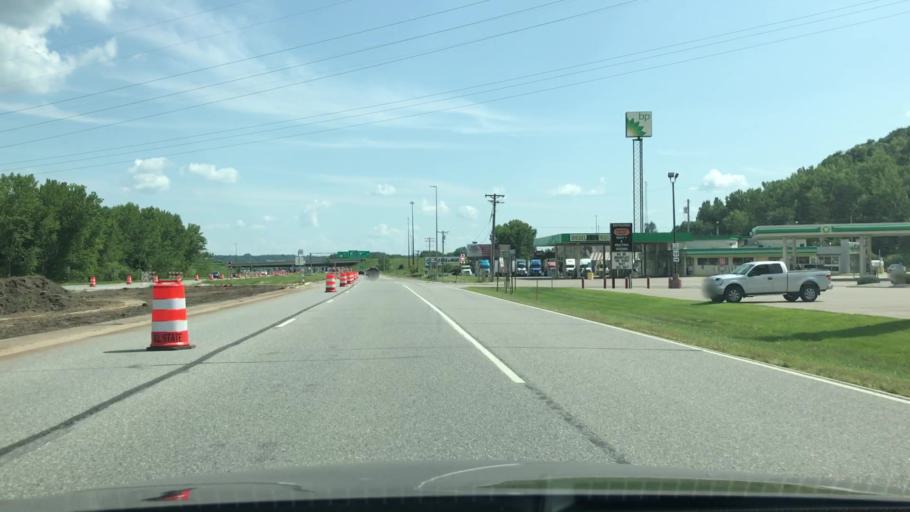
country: US
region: Minnesota
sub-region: Nicollet County
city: North Mankato
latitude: 44.1969
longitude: -94.0205
